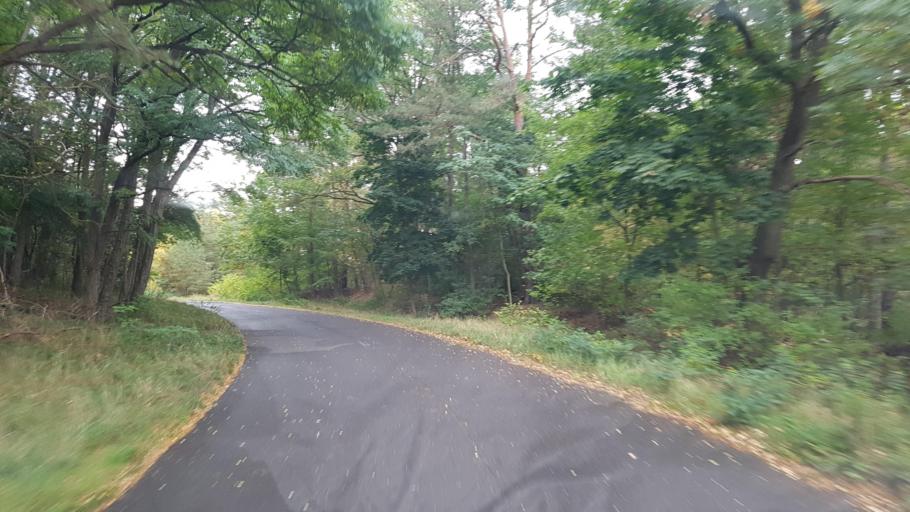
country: DE
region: Brandenburg
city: Zossen
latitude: 52.1532
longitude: 13.4850
